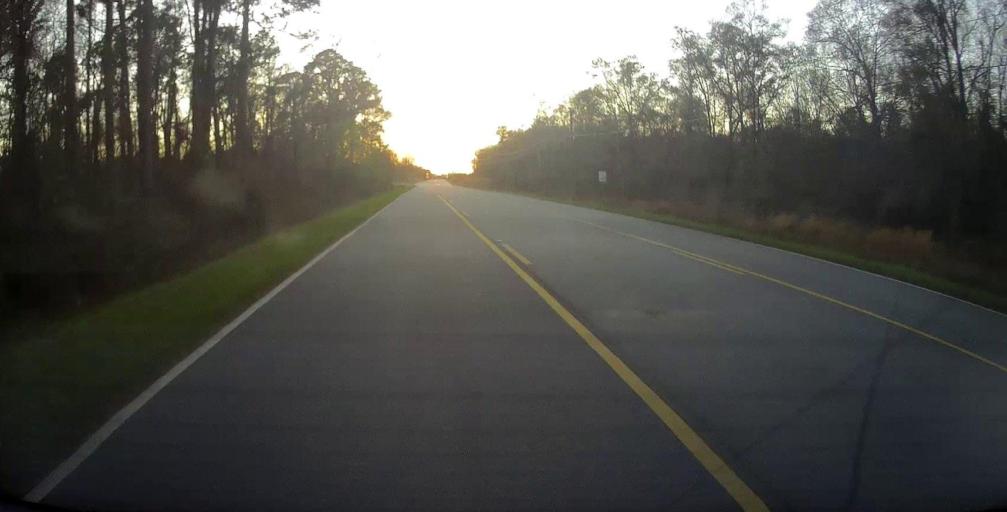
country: US
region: Georgia
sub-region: Crisp County
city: Cordele
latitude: 31.9259
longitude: -83.7530
